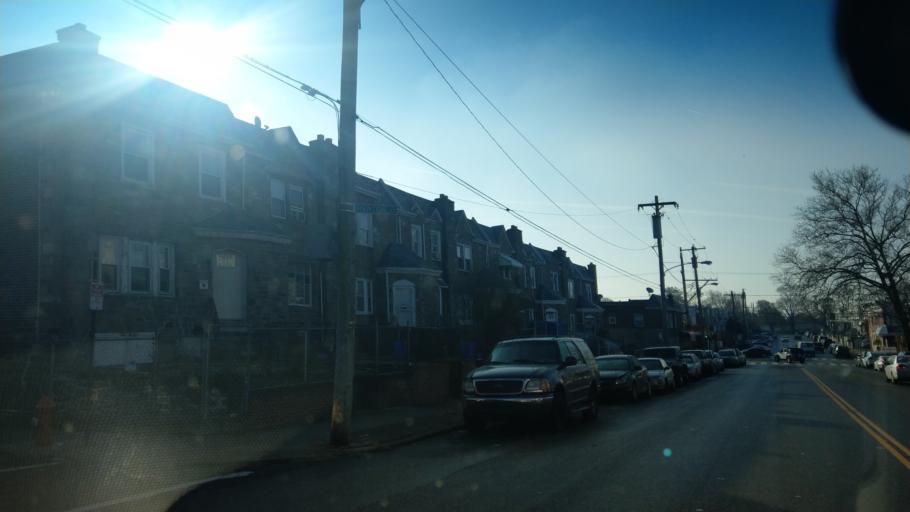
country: US
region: Pennsylvania
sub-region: Montgomery County
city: Rockledge
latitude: 40.0218
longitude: -75.1181
